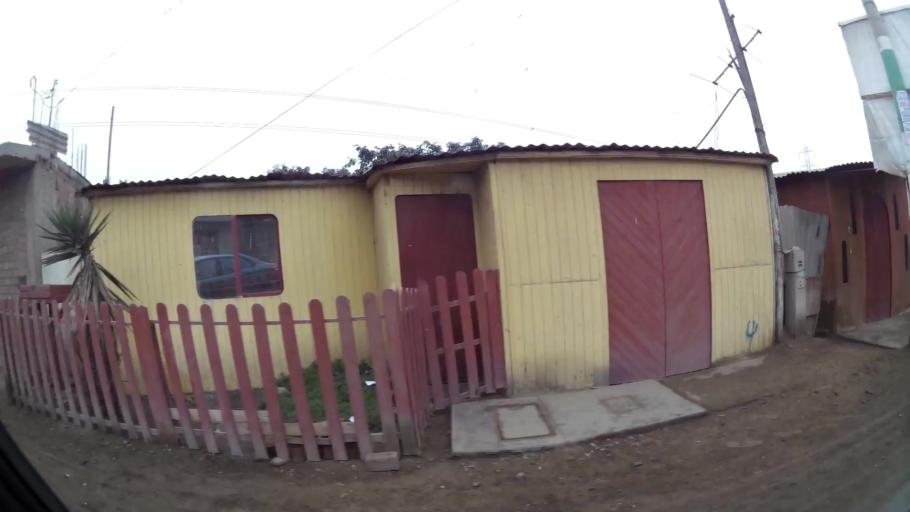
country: PE
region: Lima
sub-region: Lima
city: Urb. Santo Domingo
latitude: -11.8832
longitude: -77.0661
